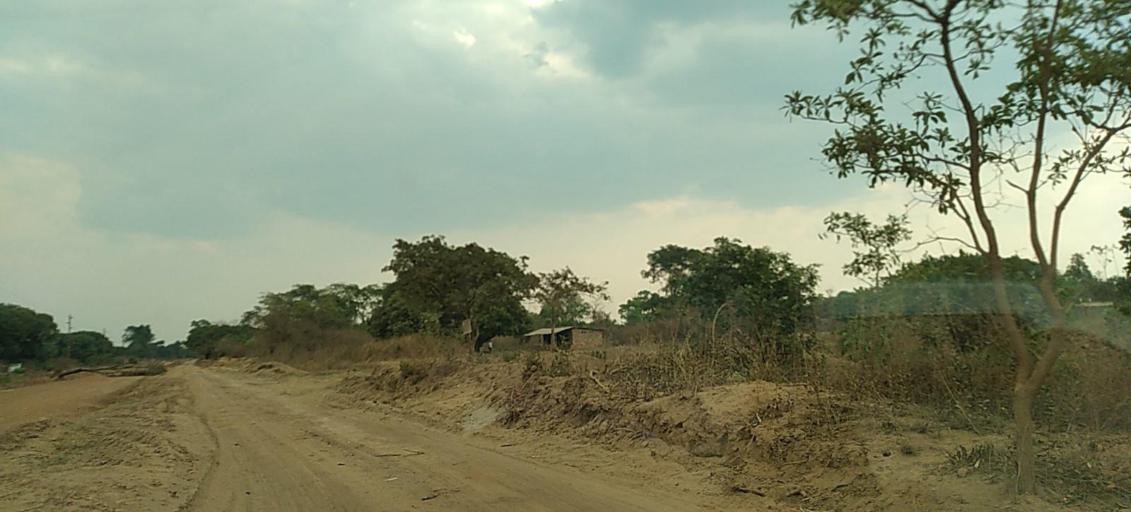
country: ZM
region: Copperbelt
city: Kalulushi
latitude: -12.8949
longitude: 27.9500
